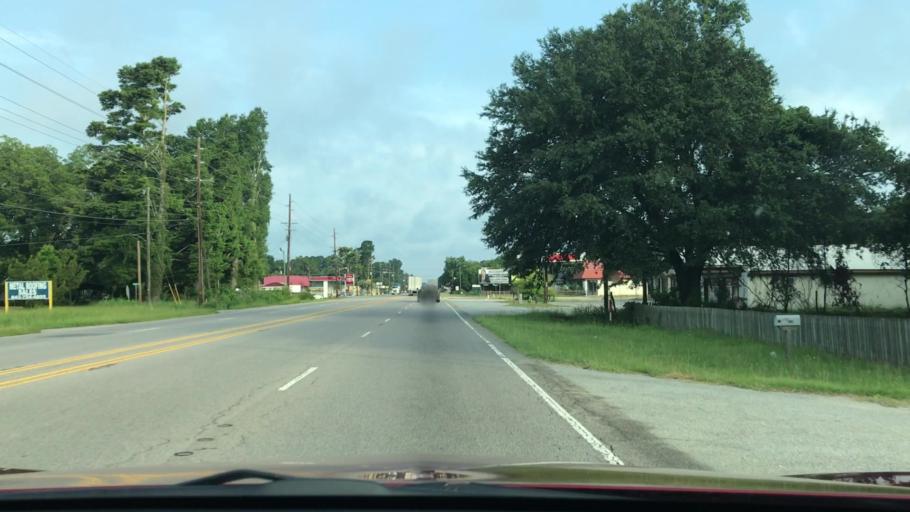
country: US
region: South Carolina
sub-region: Orangeburg County
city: Brookdale
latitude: 33.4759
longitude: -80.8139
